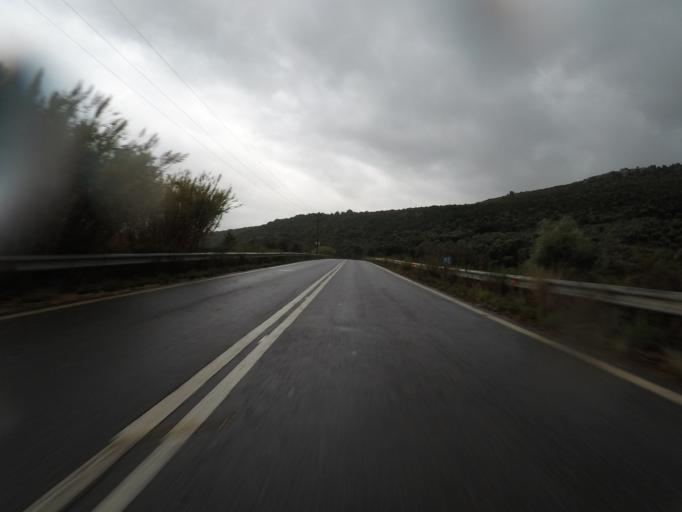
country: GR
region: Peloponnese
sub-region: Nomos Messinias
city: Pylos
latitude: 36.9317
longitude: 21.7272
